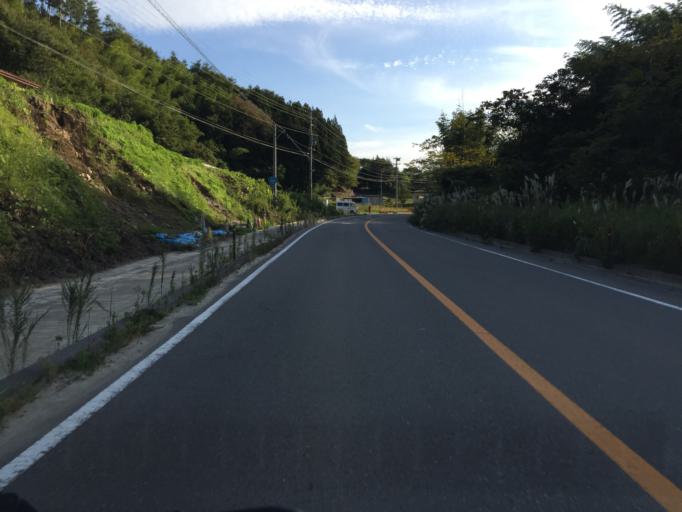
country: JP
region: Fukushima
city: Hobaramachi
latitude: 37.6839
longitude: 140.6182
